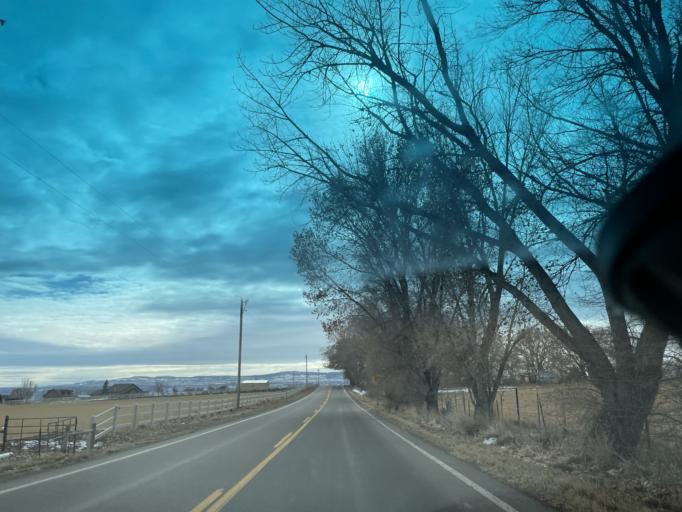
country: US
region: Colorado
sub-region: Mesa County
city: Loma
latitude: 39.2243
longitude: -108.8130
